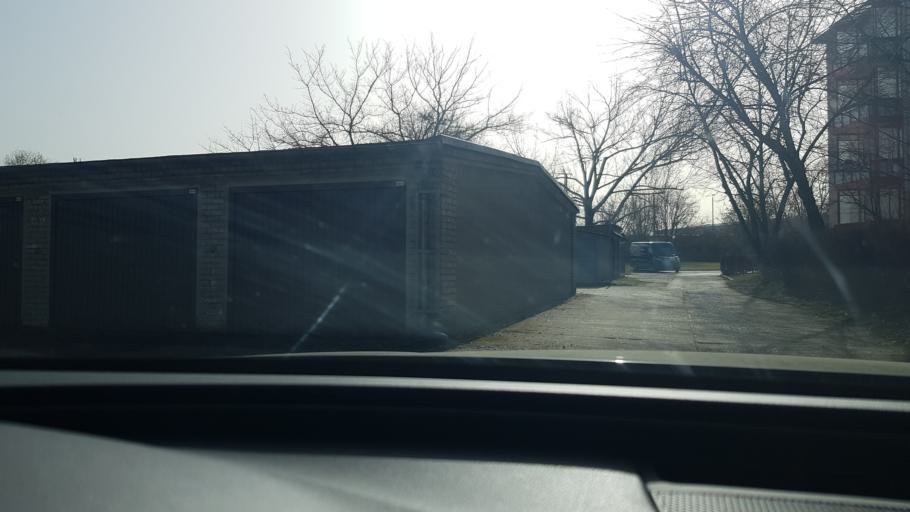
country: DE
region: Brandenburg
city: Guben
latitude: 51.9383
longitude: 14.7018
